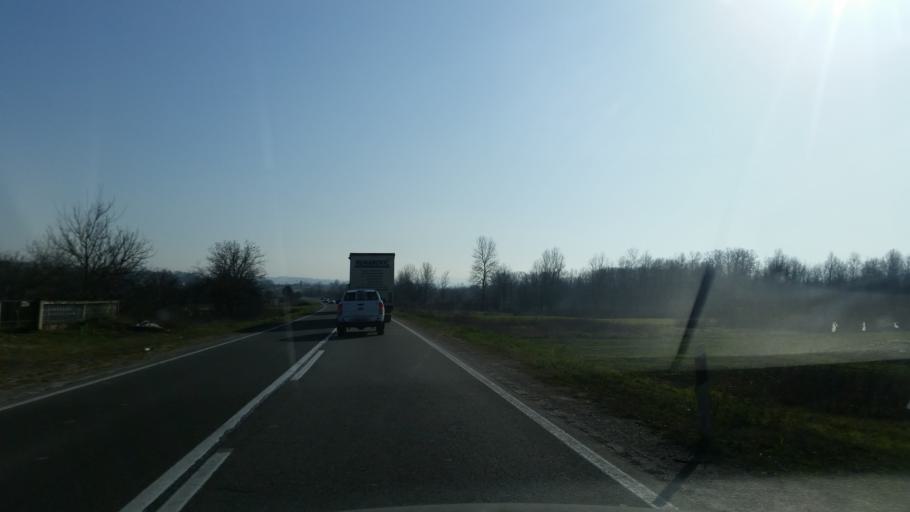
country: RS
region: Central Serbia
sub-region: Belgrade
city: Lazarevac
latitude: 44.3193
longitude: 20.2291
